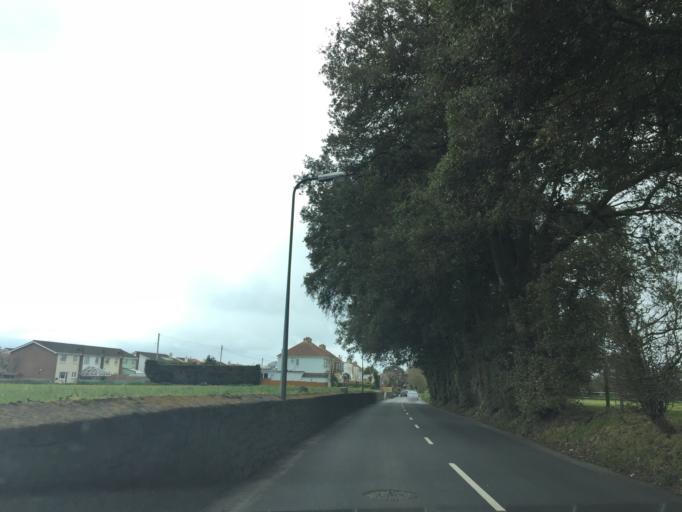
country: JE
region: St Helier
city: Saint Helier
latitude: 49.2110
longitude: -2.1418
